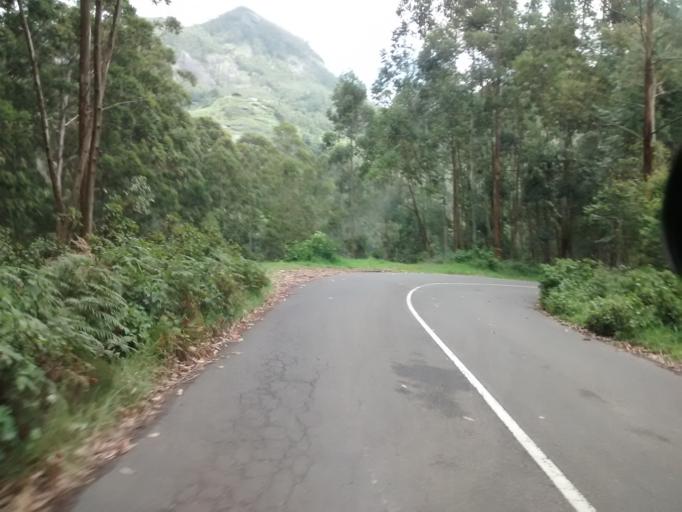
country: IN
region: Kerala
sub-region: Idukki
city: Munnar
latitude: 10.1213
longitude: 77.1456
